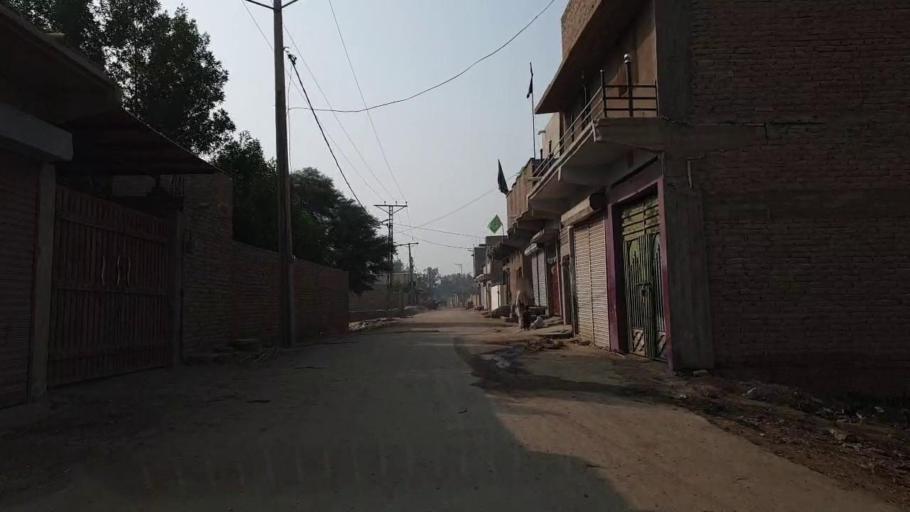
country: PK
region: Sindh
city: Sehwan
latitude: 26.4292
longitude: 67.8555
